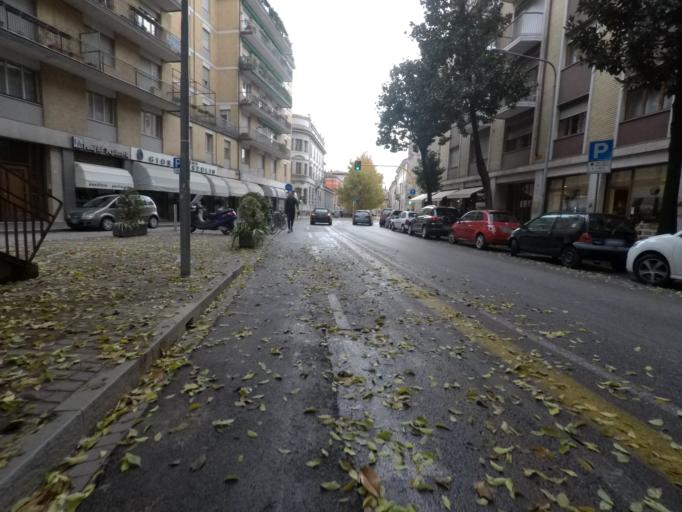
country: IT
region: Friuli Venezia Giulia
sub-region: Provincia di Udine
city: Udine
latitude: 46.0644
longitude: 13.2321
